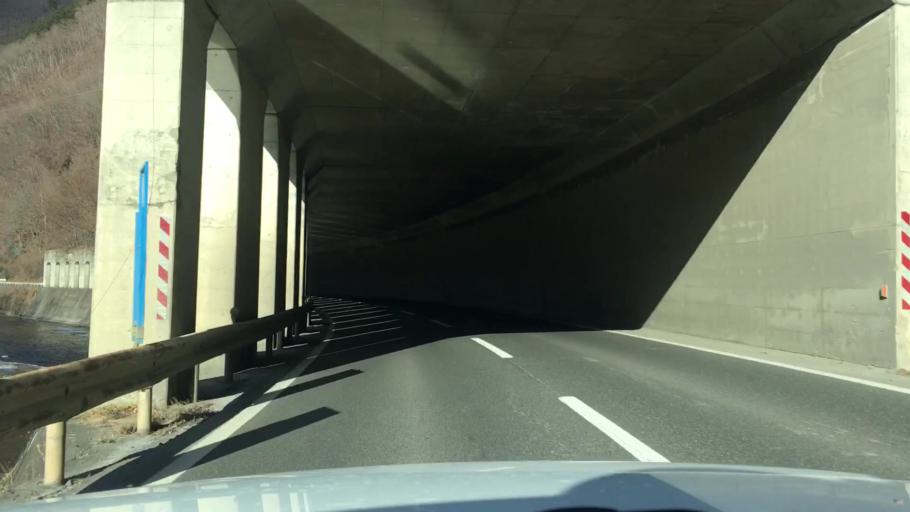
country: JP
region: Iwate
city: Miyako
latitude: 39.6049
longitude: 141.6536
